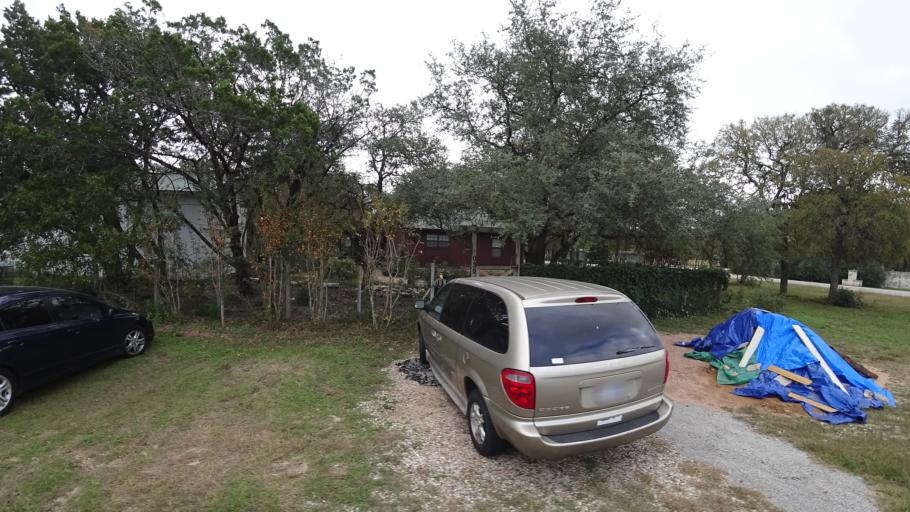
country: US
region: Texas
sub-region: Travis County
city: Bee Cave
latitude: 30.2536
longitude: -97.9220
